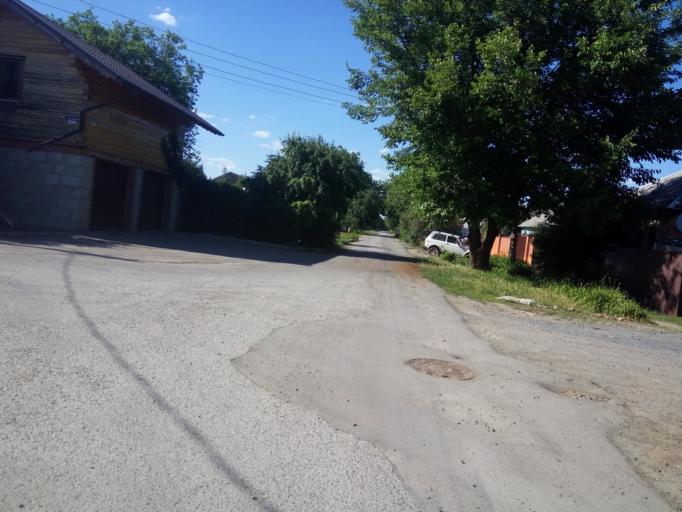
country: RU
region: Rostov
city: Bataysk
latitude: 47.1401
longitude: 39.7710
